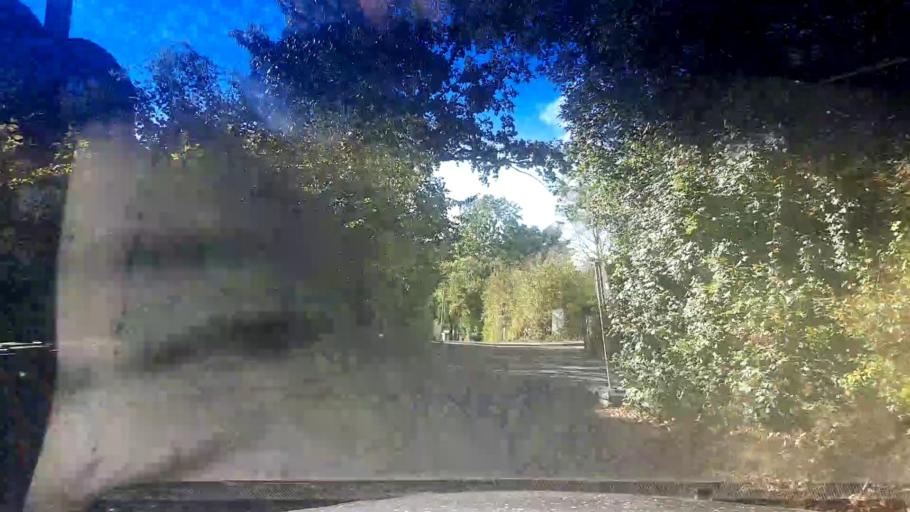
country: DE
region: Bavaria
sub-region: Upper Franconia
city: Gundelsheim
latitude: 49.9410
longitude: 10.9316
